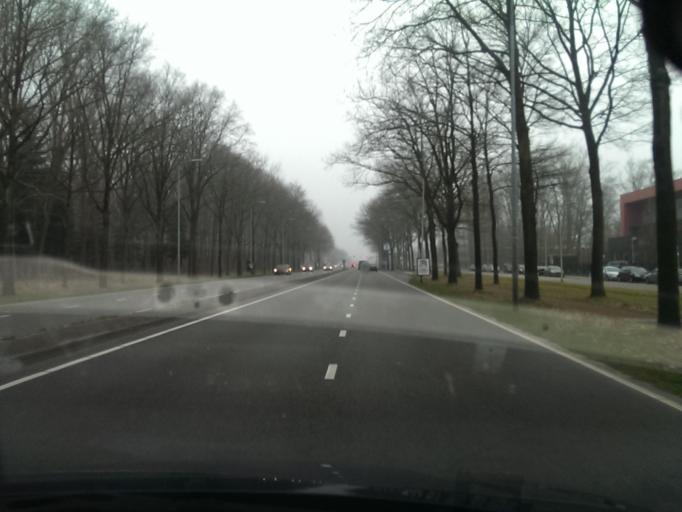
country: NL
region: North Brabant
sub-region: Gemeente Eindhoven
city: Eindhoven
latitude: 51.4712
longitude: 5.4452
